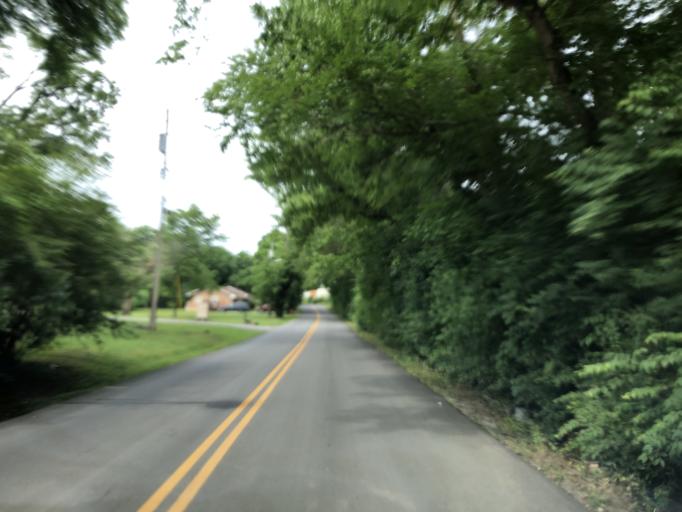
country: US
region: Tennessee
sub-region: Davidson County
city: Goodlettsville
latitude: 36.2793
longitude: -86.7056
